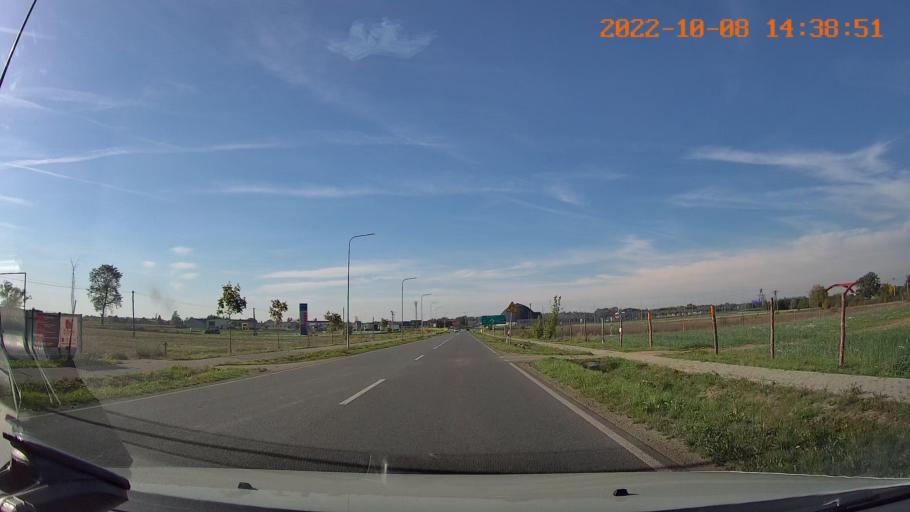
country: PL
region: Subcarpathian Voivodeship
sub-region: Powiat debicki
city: Zyrakow
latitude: 50.0724
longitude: 21.3875
